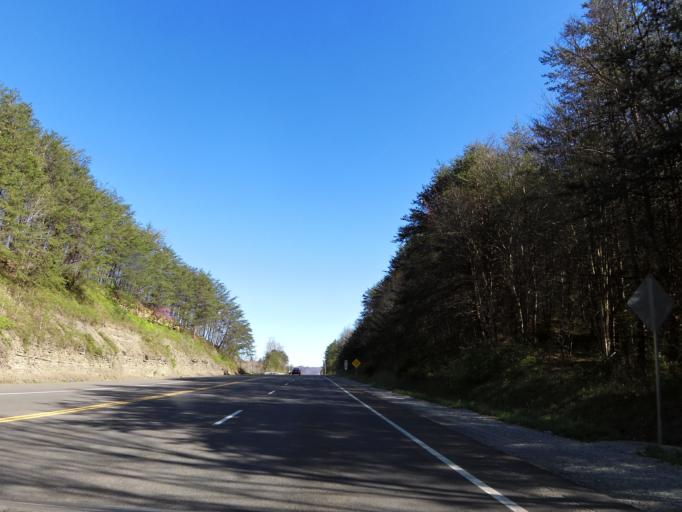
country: US
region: Tennessee
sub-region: Scott County
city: Huntsville
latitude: 36.3966
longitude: -84.4373
